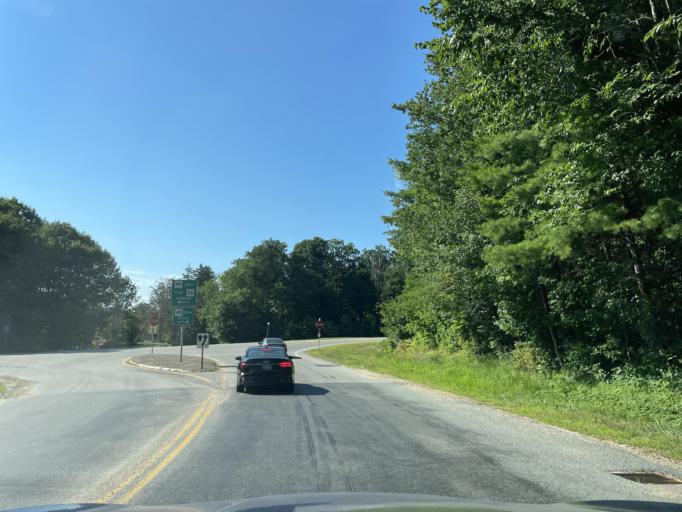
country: US
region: Massachusetts
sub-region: Worcester County
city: East Brookfield
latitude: 42.1722
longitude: -72.0303
